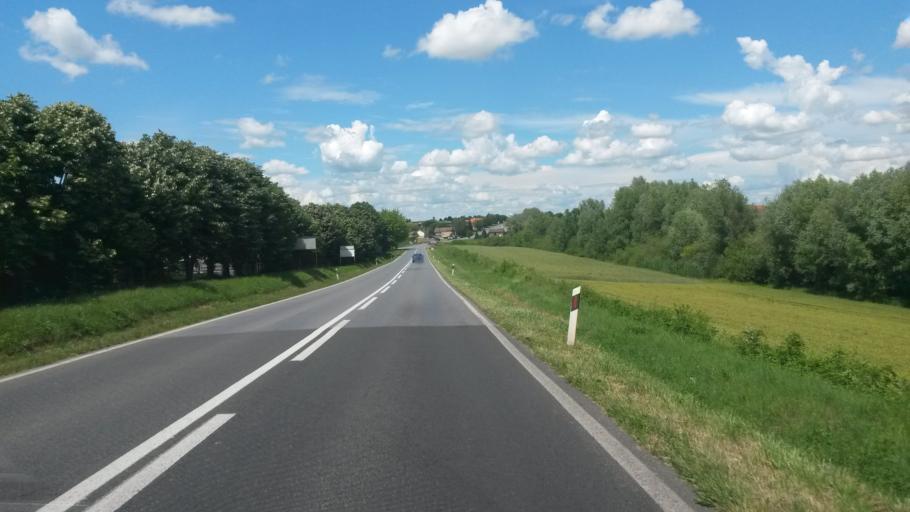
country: HR
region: Osjecko-Baranjska
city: Viskovci
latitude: 45.3395
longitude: 18.4211
